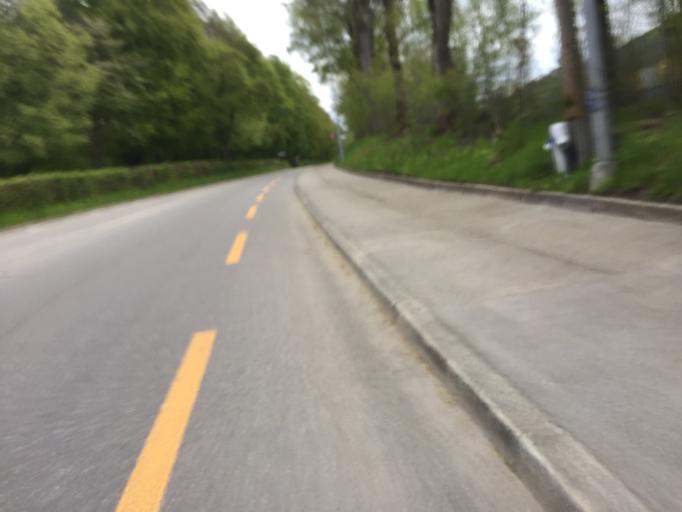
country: CH
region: Bern
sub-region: Bern-Mittelland District
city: Bern
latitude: 46.9567
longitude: 7.4242
